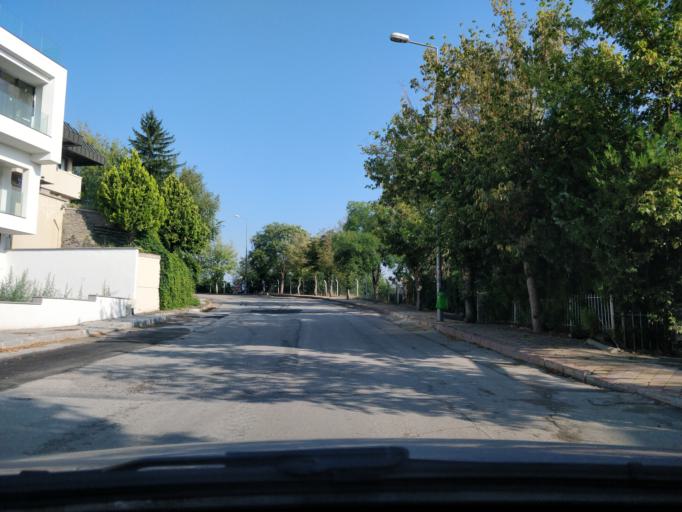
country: TR
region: Ankara
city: Batikent
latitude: 39.8960
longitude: 32.7260
